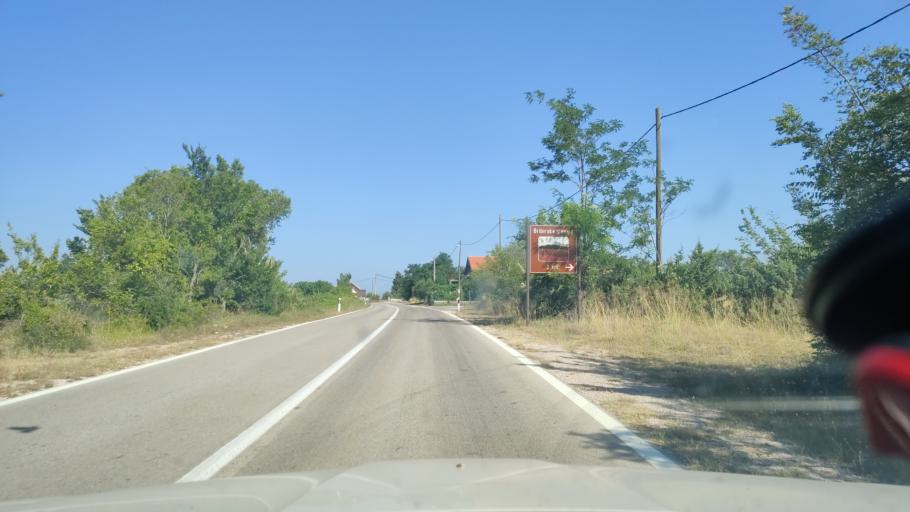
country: HR
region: Sibensko-Kniniska
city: Zaton
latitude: 43.9110
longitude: 15.8474
